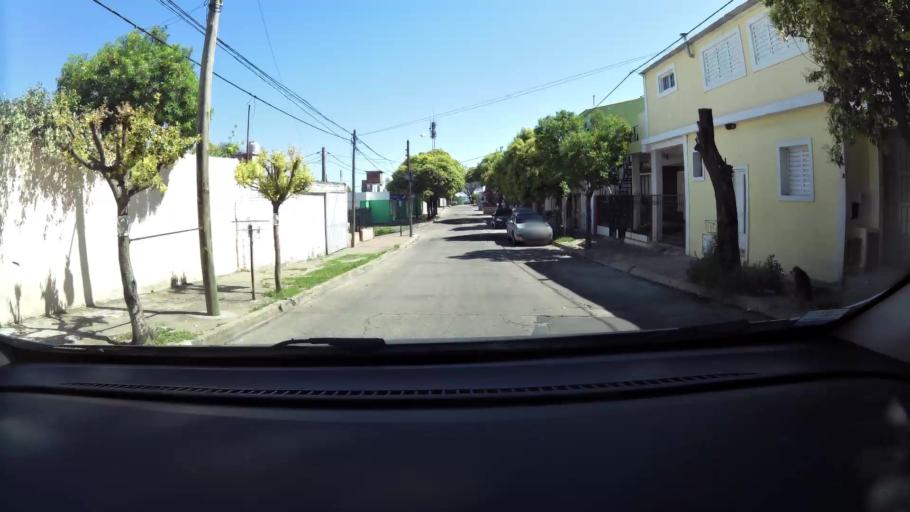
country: AR
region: Cordoba
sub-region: Departamento de Capital
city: Cordoba
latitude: -31.4308
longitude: -64.1565
